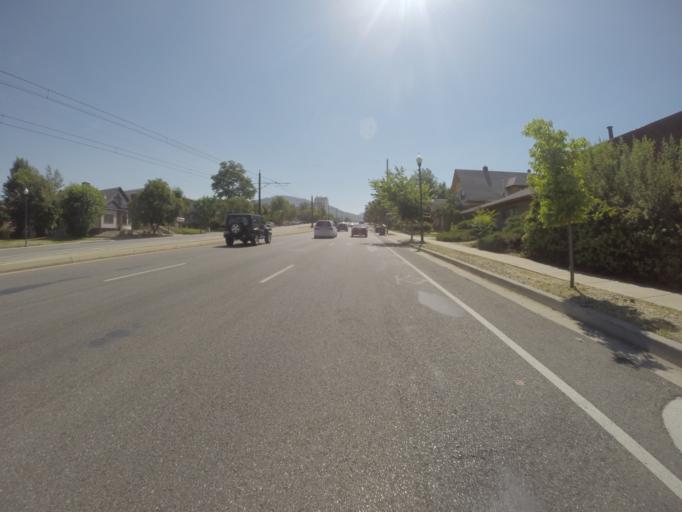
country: US
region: Utah
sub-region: Salt Lake County
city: Salt Lake City
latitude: 40.7583
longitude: -111.8595
